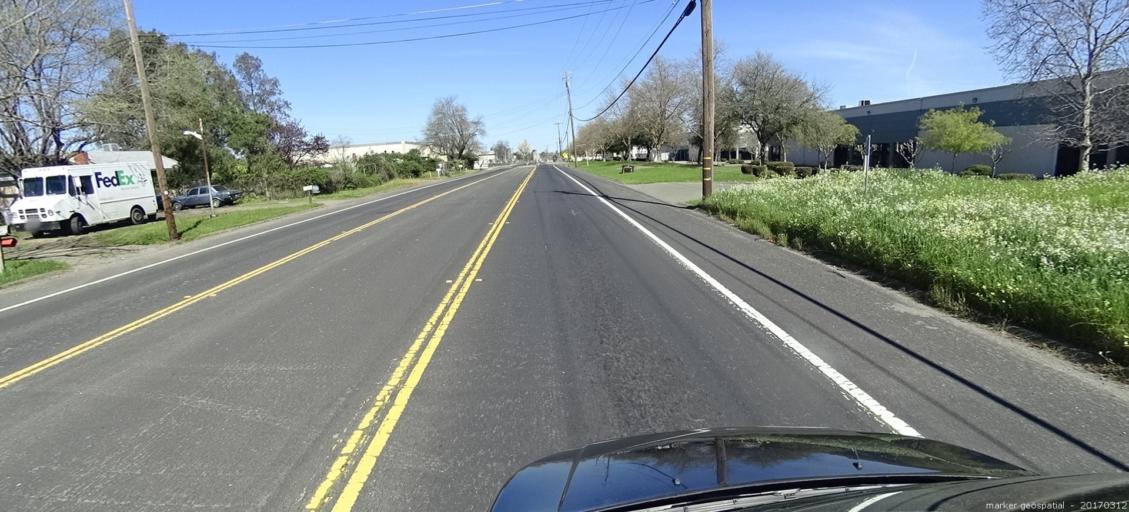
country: US
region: California
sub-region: Sacramento County
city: Rio Linda
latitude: 38.6561
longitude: -121.4291
